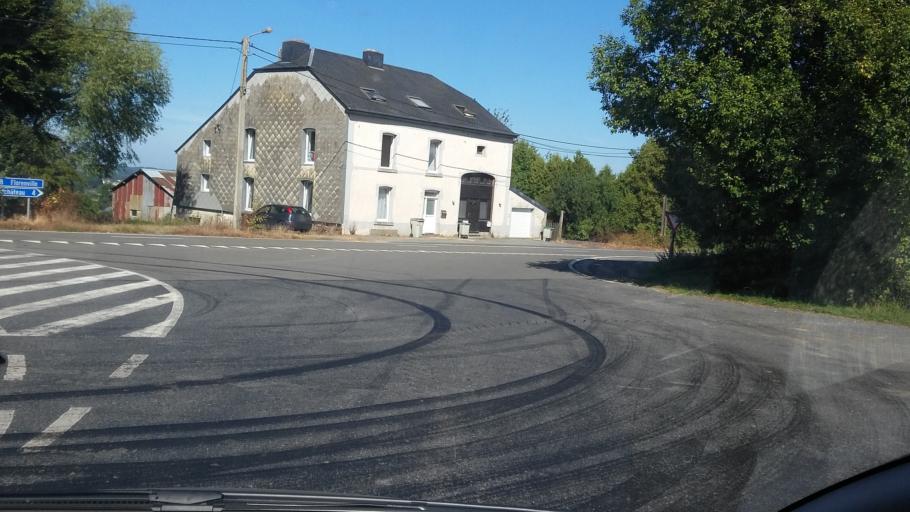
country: BE
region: Wallonia
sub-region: Province du Luxembourg
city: Neufchateau
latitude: 49.8165
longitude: 5.4157
